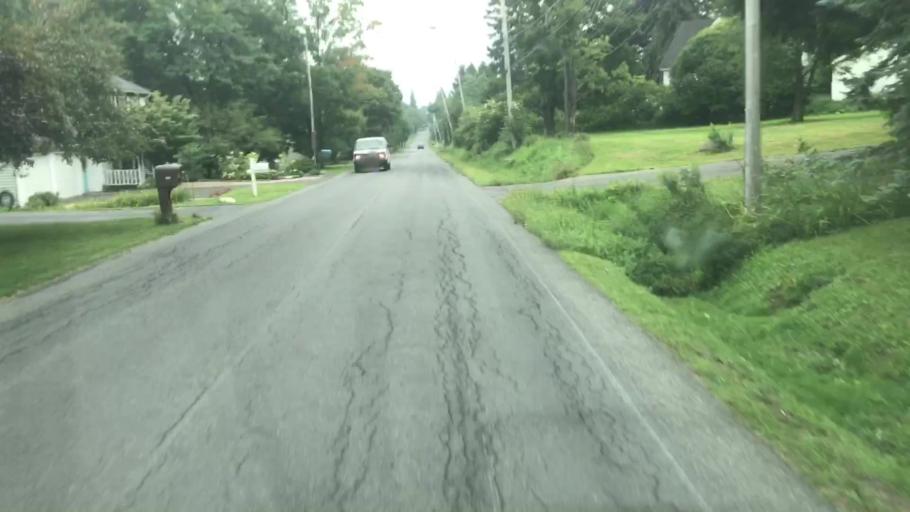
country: US
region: New York
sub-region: Onondaga County
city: Skaneateles
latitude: 42.9484
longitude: -76.4454
